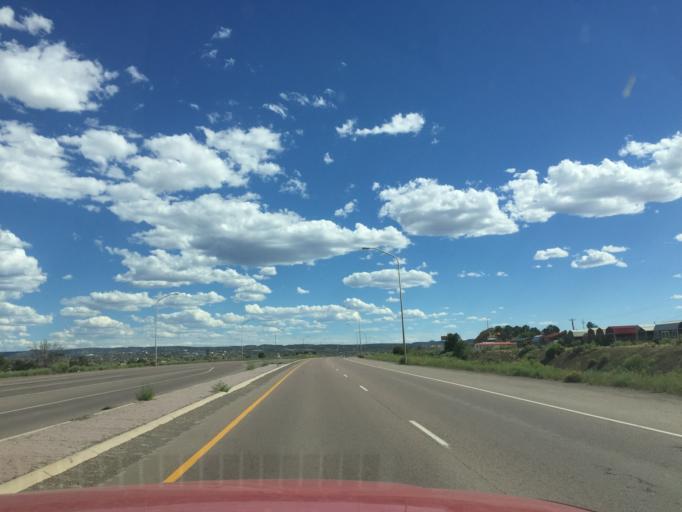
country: US
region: New Mexico
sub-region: McKinley County
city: Gallup
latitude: 35.5559
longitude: -108.7594
